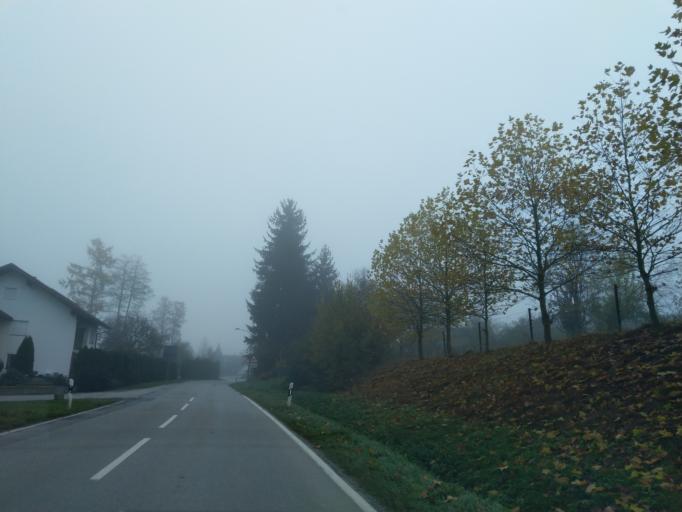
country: DE
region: Bavaria
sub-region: Lower Bavaria
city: Hengersberg
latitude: 48.7888
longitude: 13.0484
